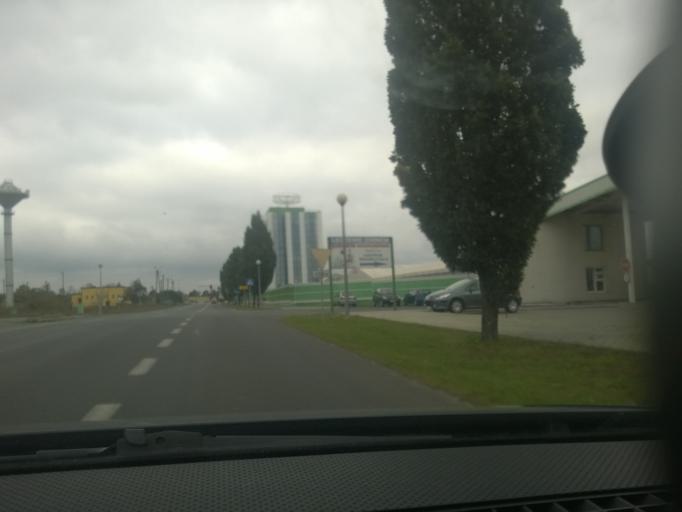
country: PL
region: Greater Poland Voivodeship
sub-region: Powiat kaliski
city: Opatowek
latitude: 51.7346
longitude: 18.1919
